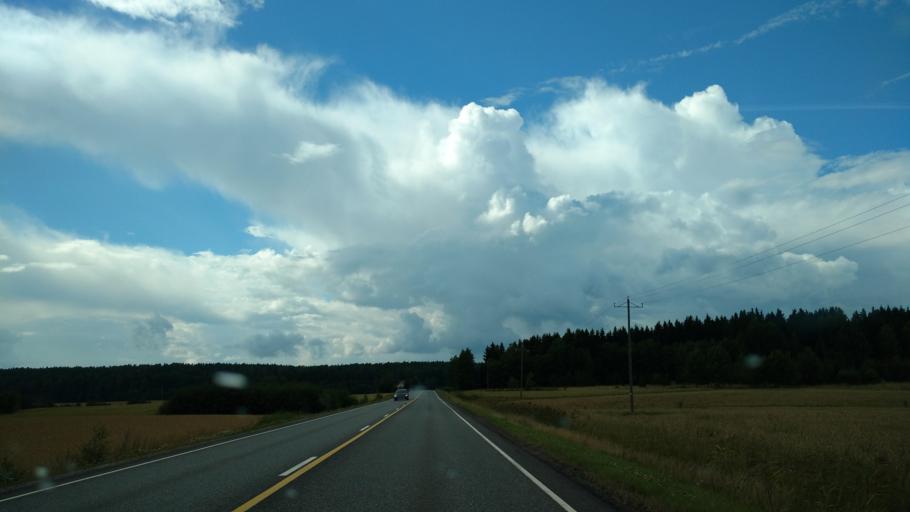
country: FI
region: Varsinais-Suomi
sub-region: Turku
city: Sauvo
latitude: 60.4077
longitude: 22.8010
